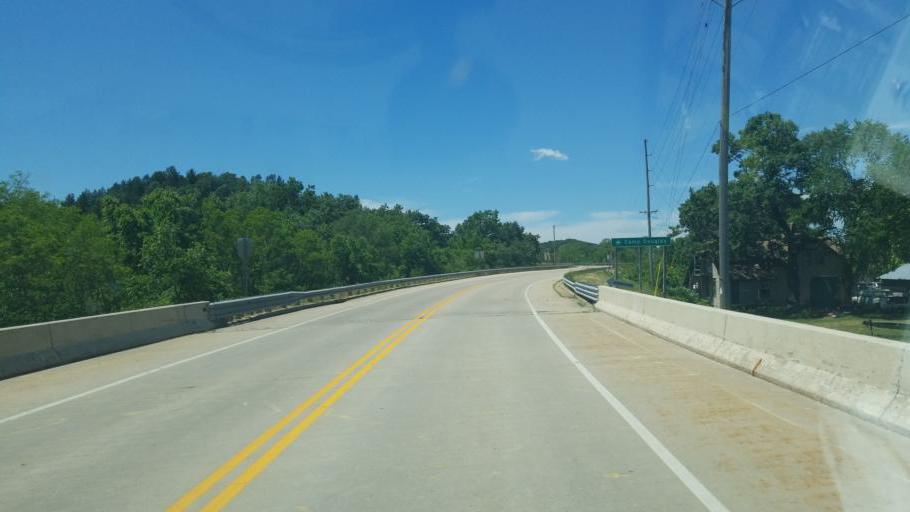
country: US
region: Wisconsin
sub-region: Juneau County
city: New Lisbon
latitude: 43.9227
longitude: -90.2691
